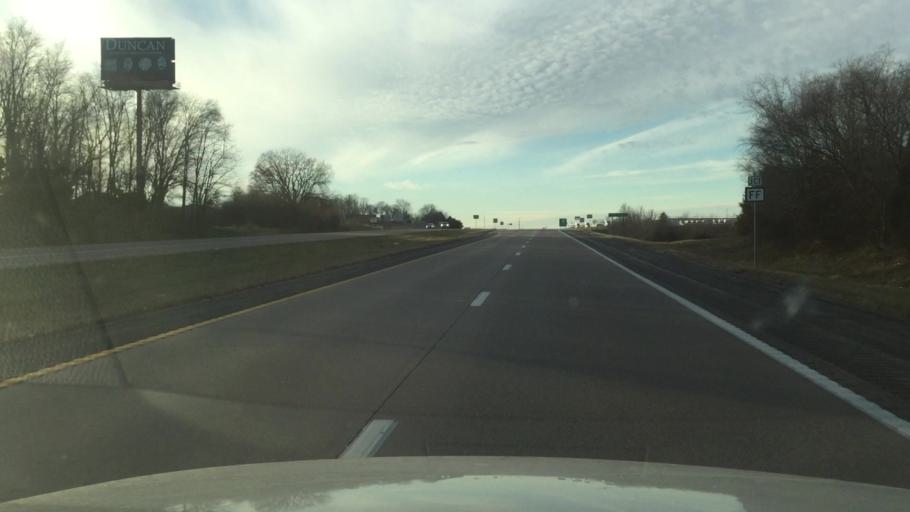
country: US
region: Missouri
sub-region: Miller County
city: Eldon
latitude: 38.3688
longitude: -92.5194
